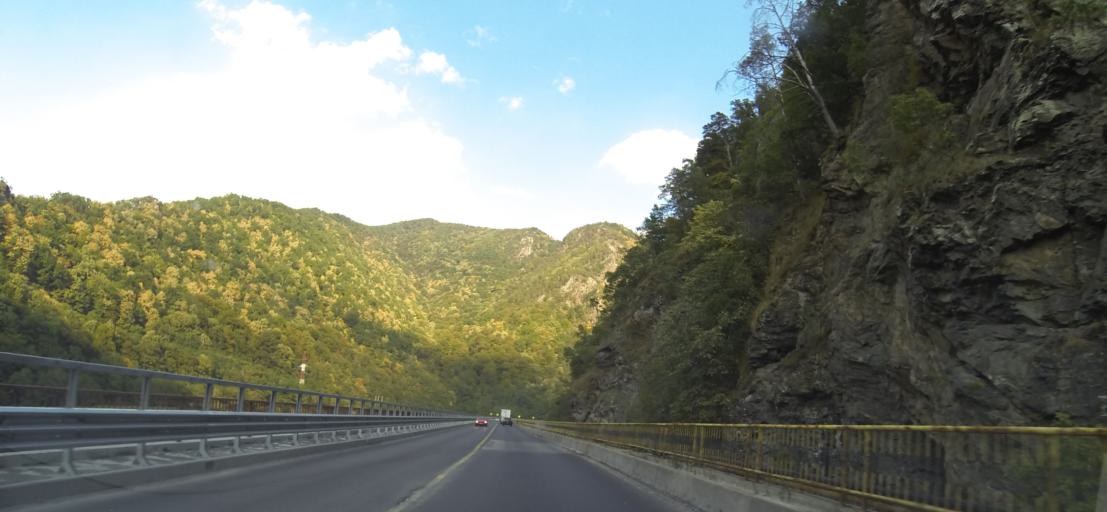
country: RO
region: Valcea
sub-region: Comuna Brezoi
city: Brezoi
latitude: 45.2989
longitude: 24.2860
